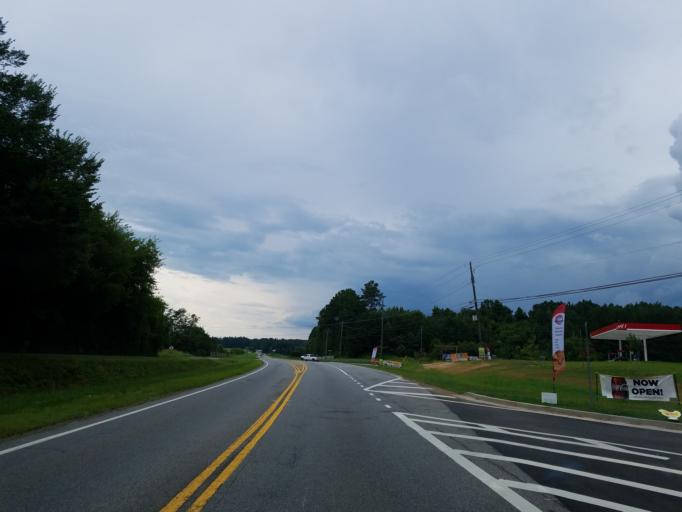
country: US
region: Georgia
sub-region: Bartow County
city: Cartersville
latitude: 34.2645
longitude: -84.8613
